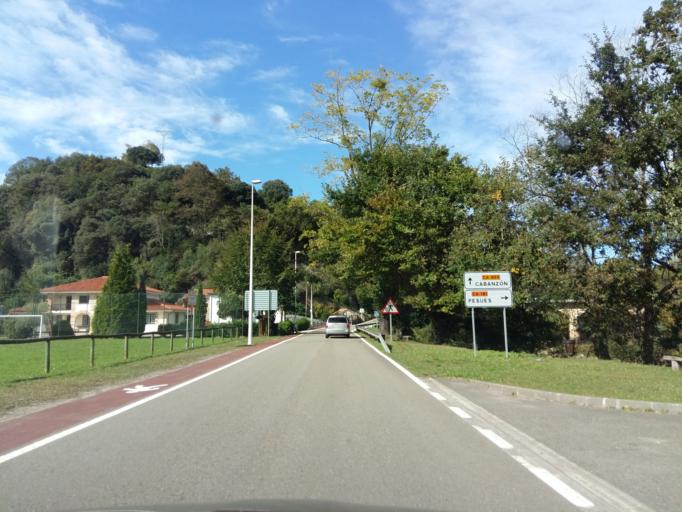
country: ES
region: Cantabria
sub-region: Provincia de Cantabria
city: San Vicente de la Barquera
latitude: 43.3069
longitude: -4.4703
